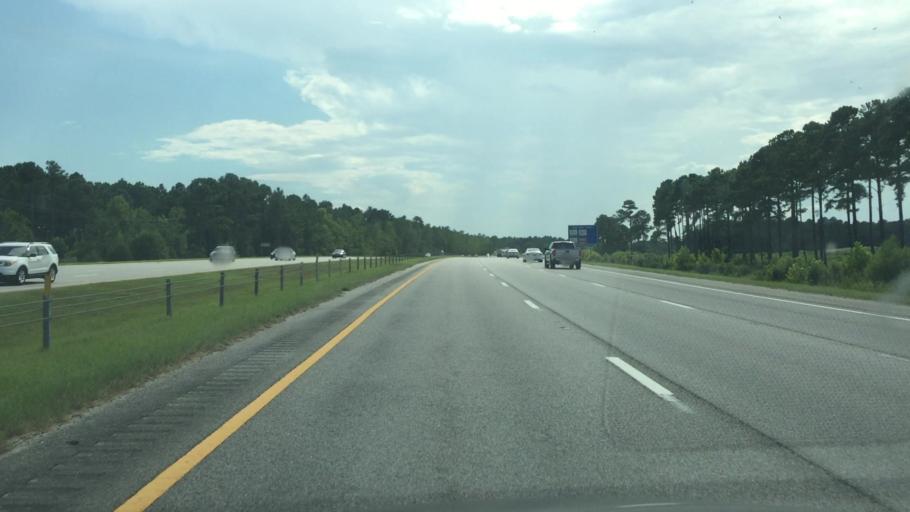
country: US
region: South Carolina
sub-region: Horry County
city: Myrtle Beach
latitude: 33.7590
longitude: -78.8425
